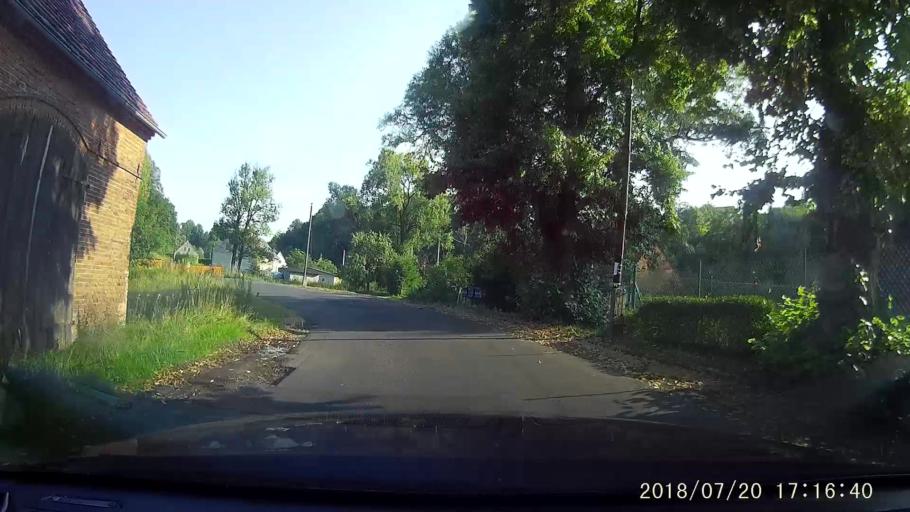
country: PL
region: Lower Silesian Voivodeship
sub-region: Powiat lubanski
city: Lesna
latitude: 51.0007
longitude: 15.2829
